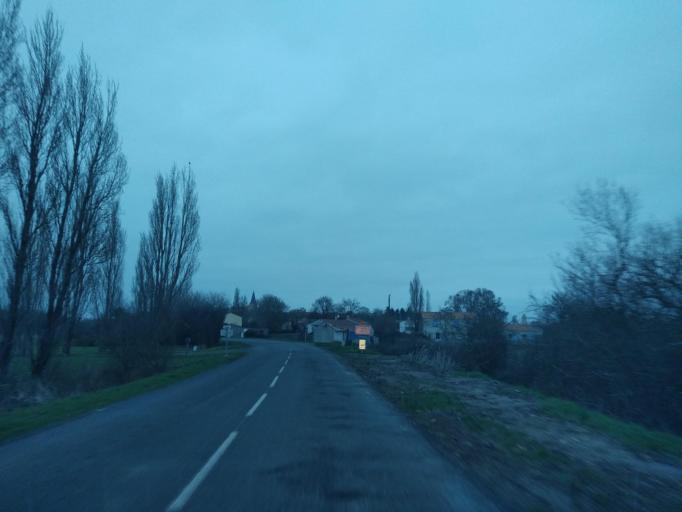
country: FR
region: Pays de la Loire
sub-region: Departement de la Vendee
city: Triaize
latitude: 46.4022
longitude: -1.2663
